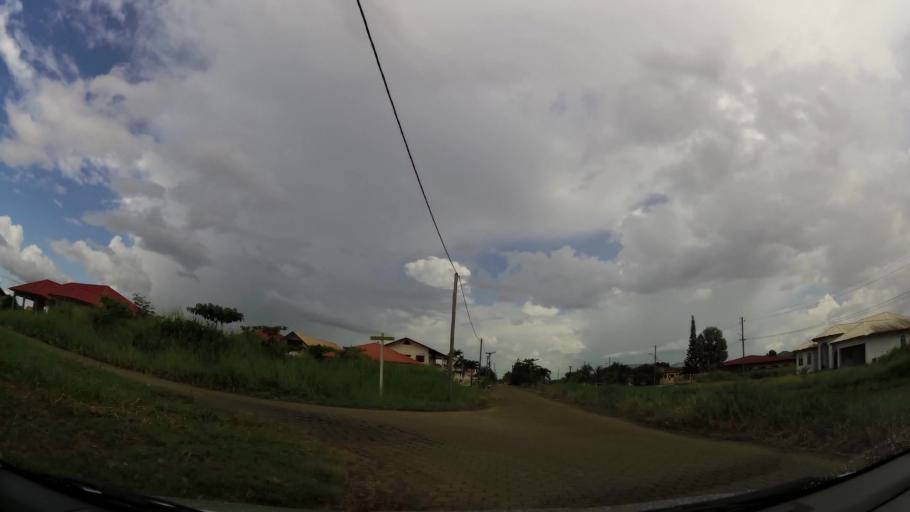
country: SR
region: Commewijne
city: Nieuw Amsterdam
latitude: 5.8634
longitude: -55.1226
